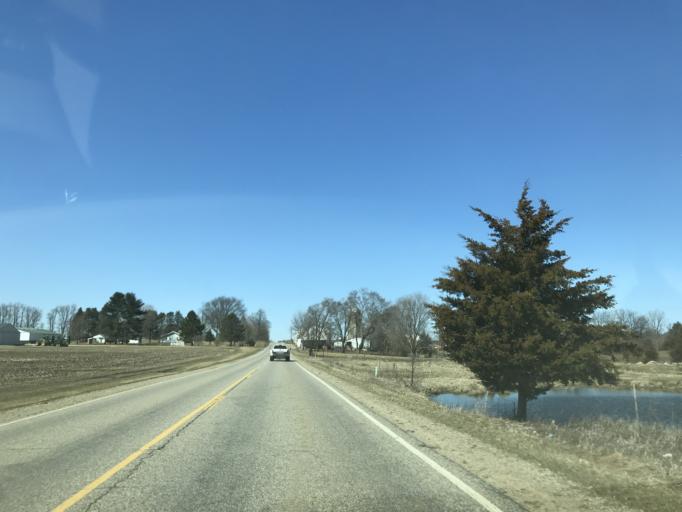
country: US
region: Michigan
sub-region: Hillsdale County
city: Litchfield
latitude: 41.9857
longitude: -84.7955
